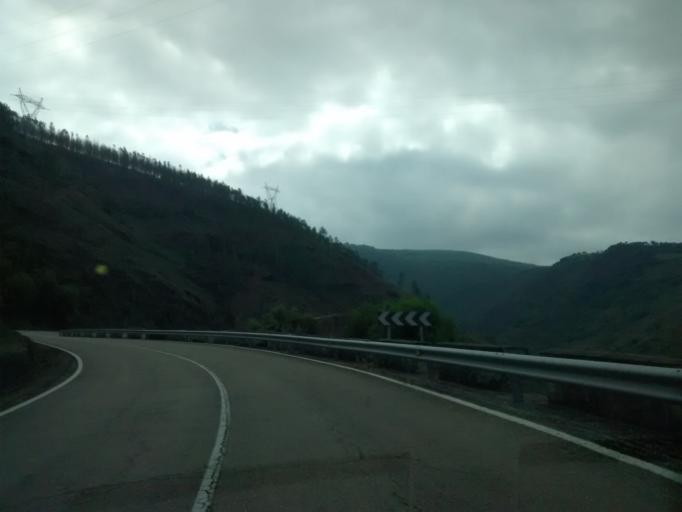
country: ES
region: Galicia
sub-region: Provincia de Ourense
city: Manzaneda
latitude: 42.3300
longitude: -7.2121
